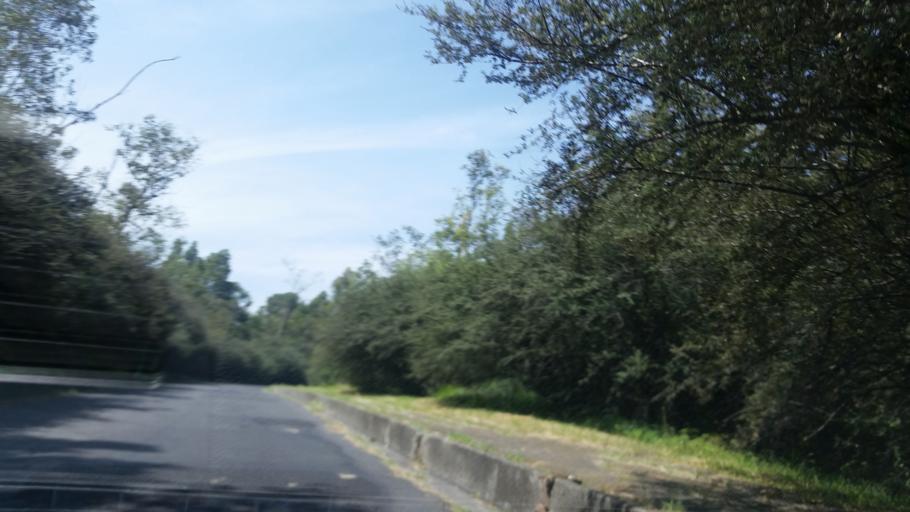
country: MX
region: Mexico City
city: Polanco
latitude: 19.4075
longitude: -99.2133
